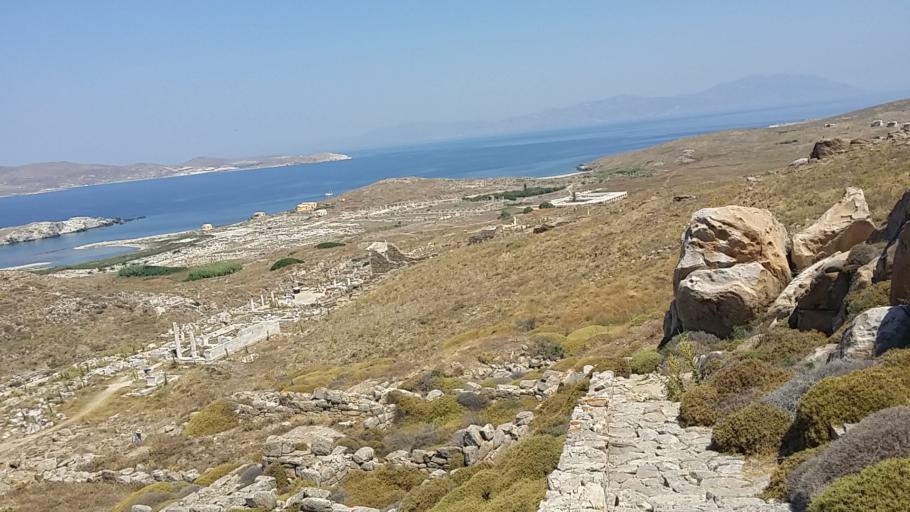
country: GR
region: South Aegean
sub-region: Nomos Kykladon
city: Mykonos
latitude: 37.3964
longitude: 25.2717
